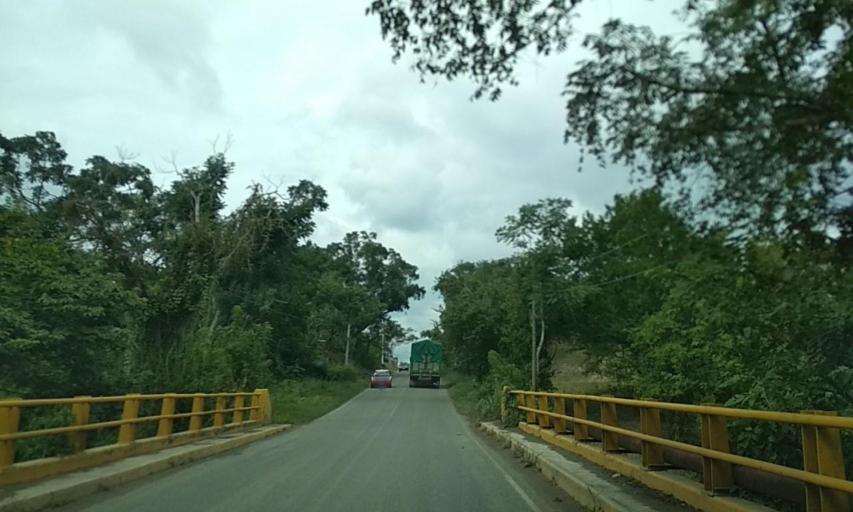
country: MX
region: Veracruz
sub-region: Papantla
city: El Chote
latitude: 20.3700
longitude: -97.3332
